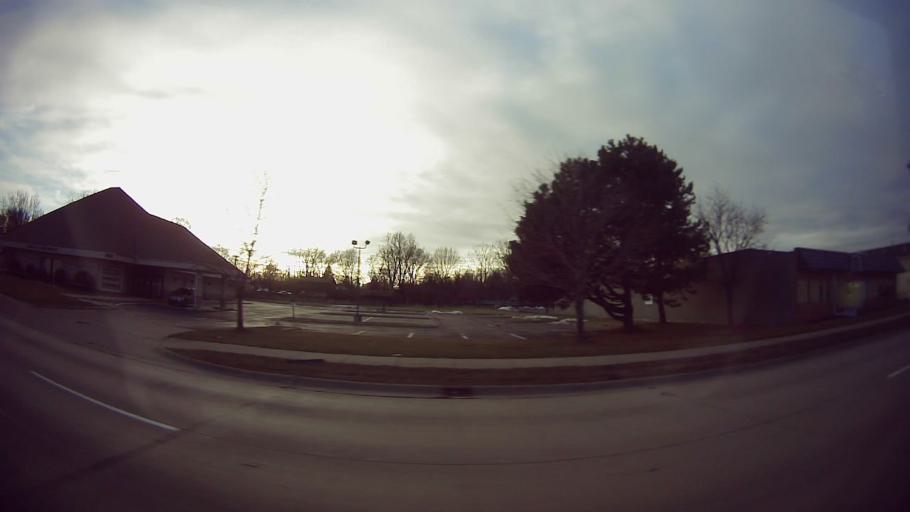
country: US
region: Michigan
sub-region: Wayne County
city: Taylor
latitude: 42.2433
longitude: -83.2698
